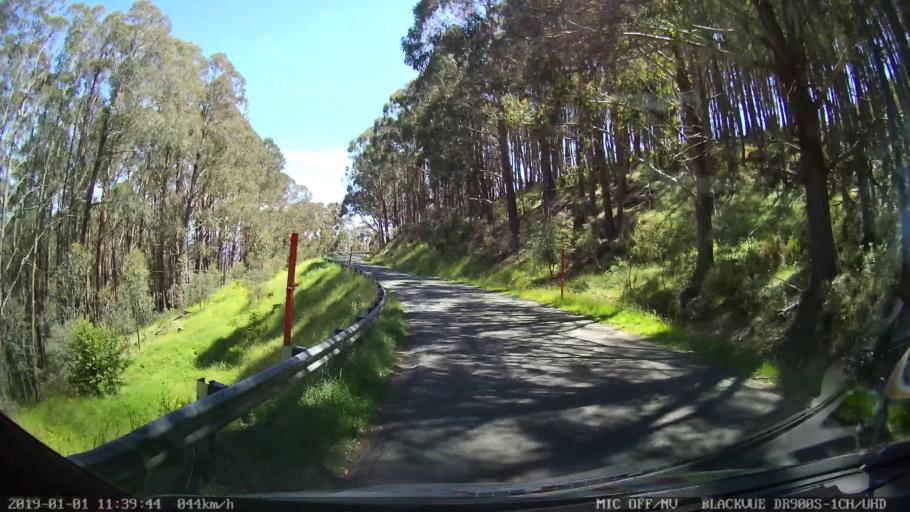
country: AU
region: New South Wales
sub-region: Snowy River
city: Jindabyne
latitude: -35.9248
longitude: 148.3860
